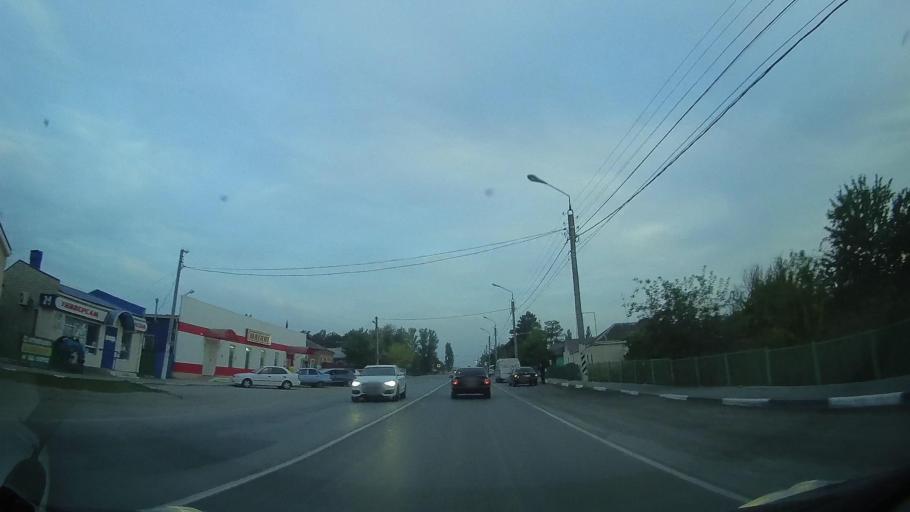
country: RU
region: Rostov
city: Kagal'nitskaya
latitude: 46.8800
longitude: 40.1524
